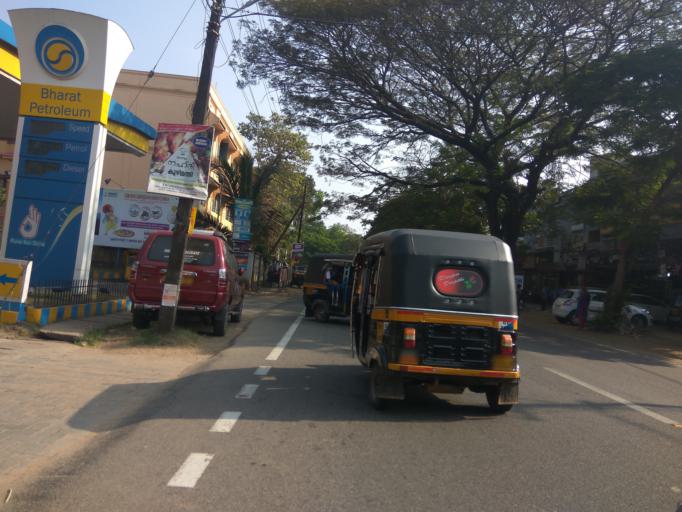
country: IN
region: Kerala
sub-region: Kozhikode
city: Kozhikode
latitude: 11.2850
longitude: 75.7685
